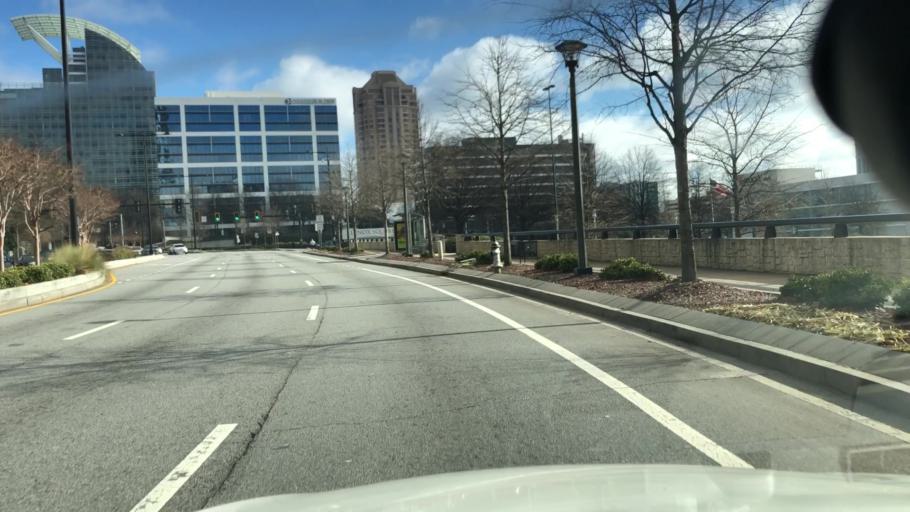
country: US
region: Georgia
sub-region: DeKalb County
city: North Atlanta
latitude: 33.8489
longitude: -84.3644
